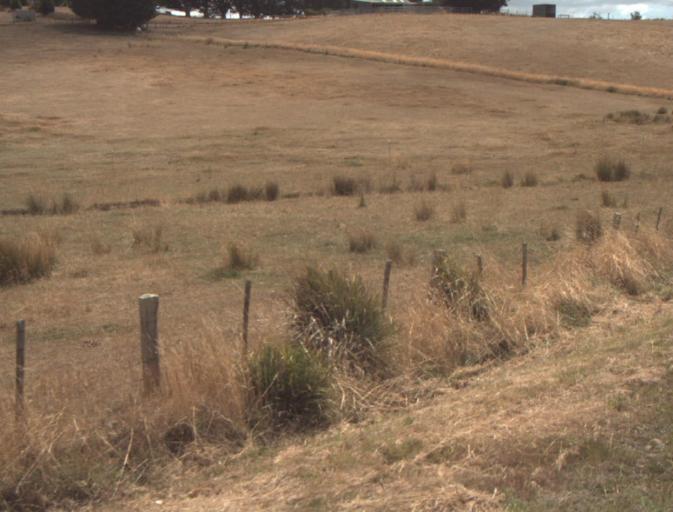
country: AU
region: Tasmania
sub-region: Launceston
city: Mayfield
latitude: -41.2096
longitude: 147.1199
